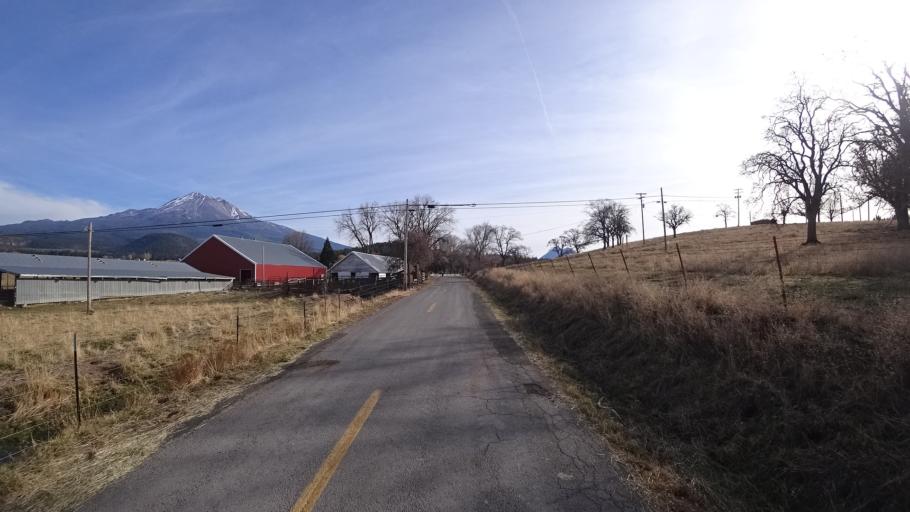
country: US
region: California
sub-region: Siskiyou County
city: Weed
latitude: 41.4565
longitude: -122.3848
